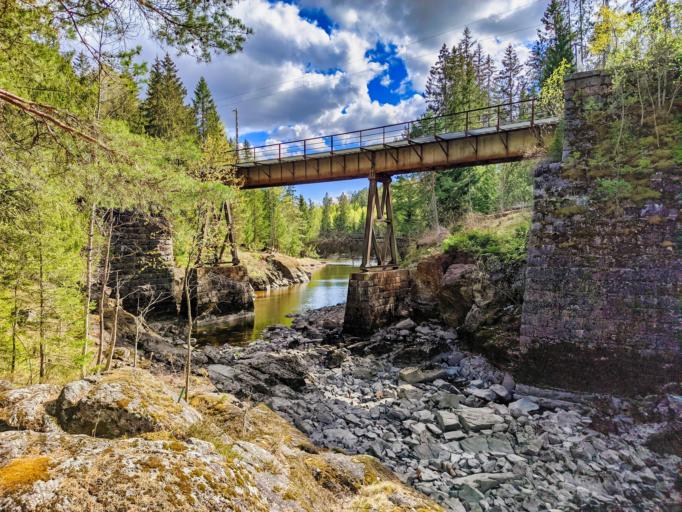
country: NO
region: Ostfold
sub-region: Spydeberg
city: Spydeberg
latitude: 59.6081
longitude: 11.1183
